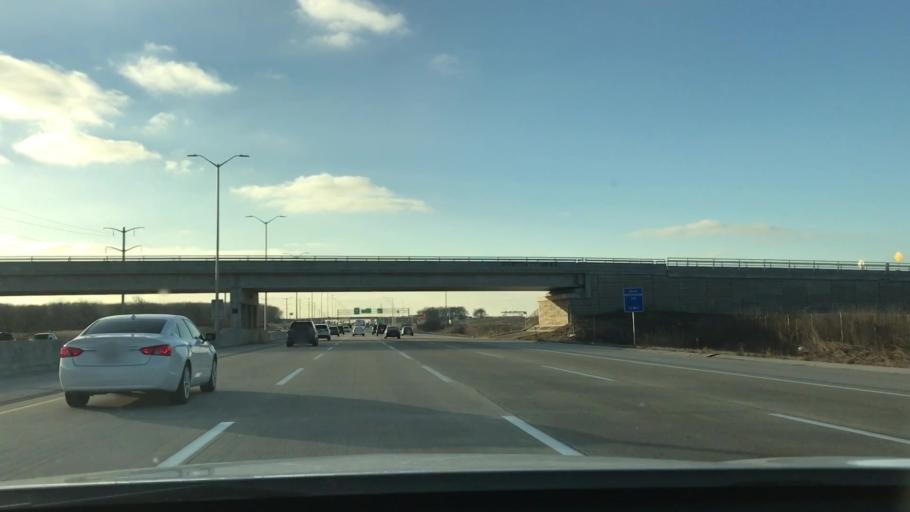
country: US
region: Illinois
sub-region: Cook County
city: Streamwood
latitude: 42.0670
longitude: -88.1783
